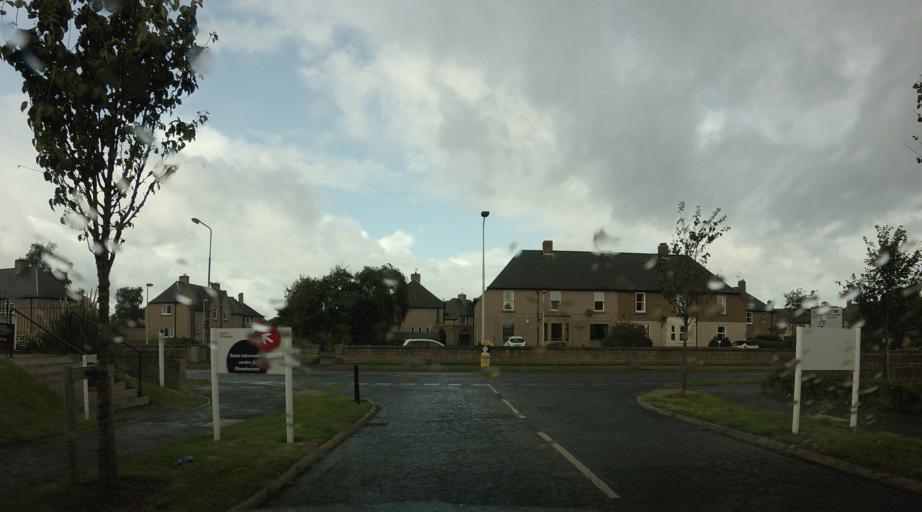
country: GB
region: Scotland
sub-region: East Lothian
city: Musselburgh
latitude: 55.9430
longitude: -3.0283
